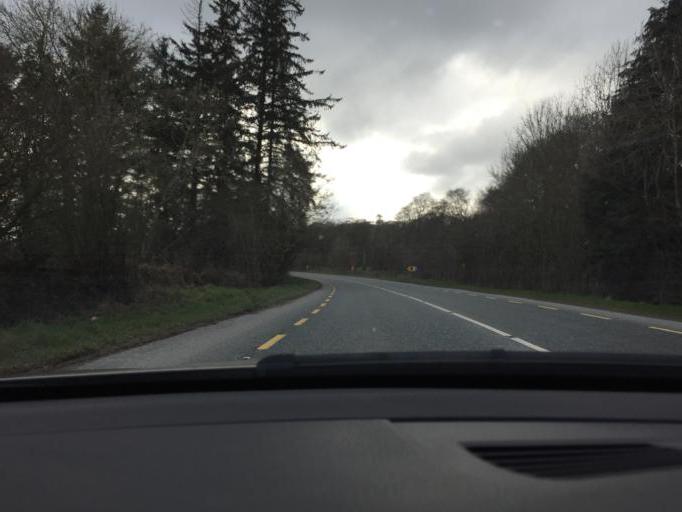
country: IE
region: Leinster
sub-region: South Dublin
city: Rathcoole
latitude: 53.2144
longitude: -6.4795
